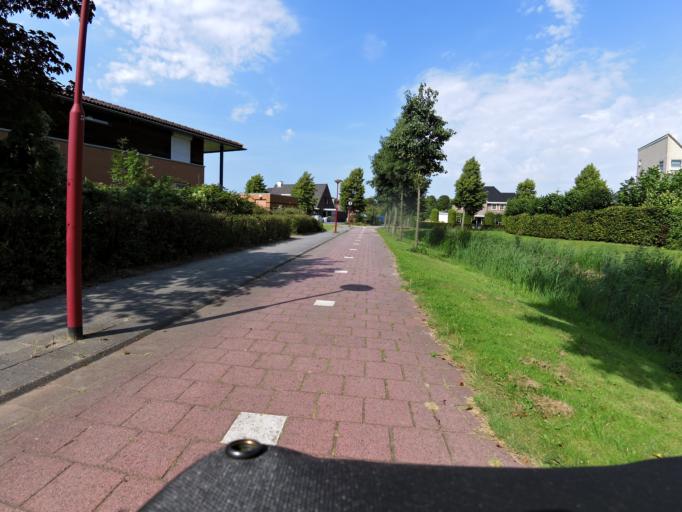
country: NL
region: South Holland
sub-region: Gemeente Oud-Beijerland
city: Oud-Beijerland
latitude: 51.8201
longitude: 4.4310
